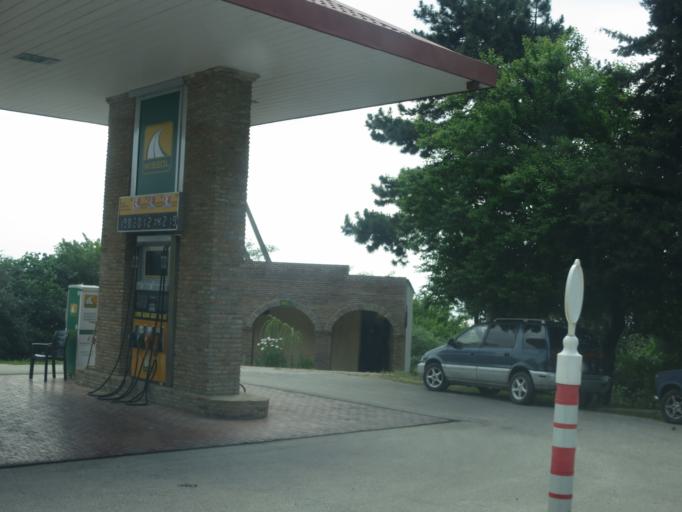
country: GE
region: Kakheti
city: Sighnaghi
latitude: 41.6116
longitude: 45.9237
